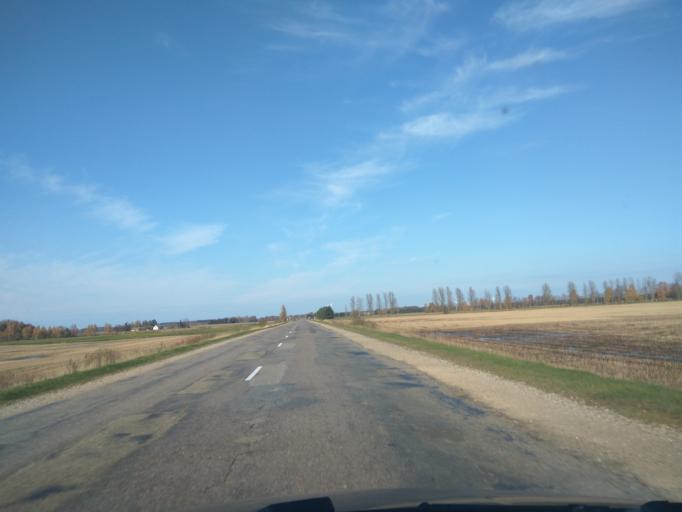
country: LV
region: Ventspils Rajons
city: Piltene
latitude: 57.2497
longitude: 21.5926
